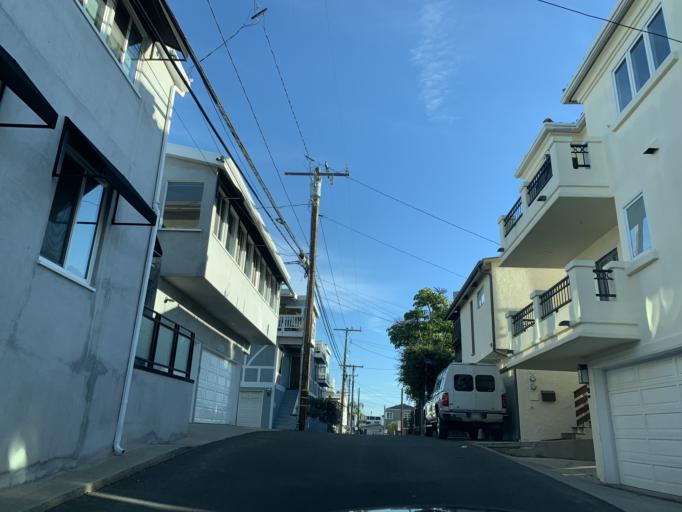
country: US
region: California
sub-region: Los Angeles County
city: Manhattan Beach
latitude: 33.8782
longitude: -118.4057
